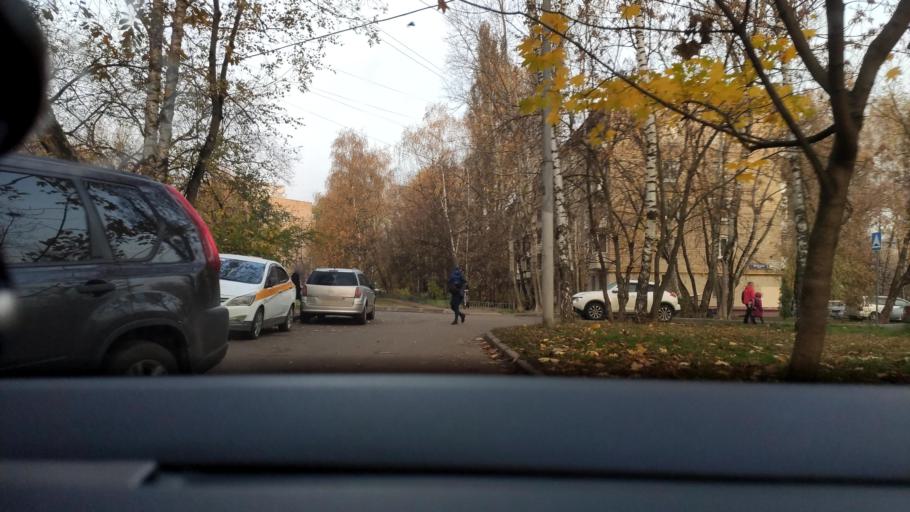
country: RU
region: Moskovskaya
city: Bol'shaya Setun'
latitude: 55.7374
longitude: 37.4042
